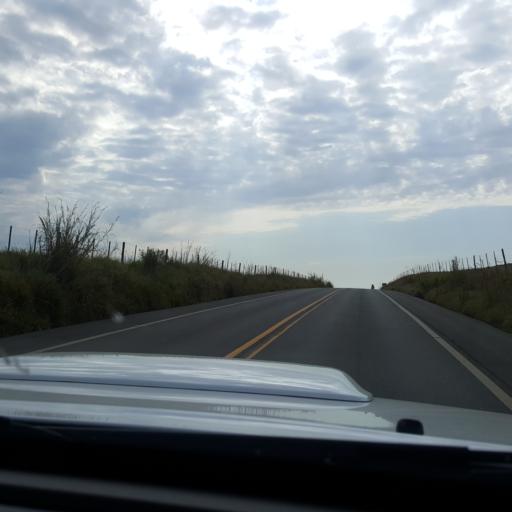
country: BR
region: Sao Paulo
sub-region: Itaporanga
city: Itaporanga
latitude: -23.7642
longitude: -49.4476
